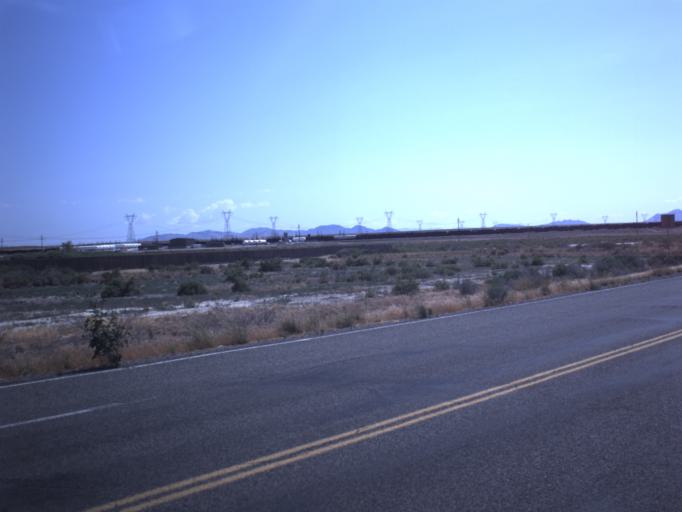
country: US
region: Utah
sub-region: Millard County
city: Delta
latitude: 39.4937
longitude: -112.5726
